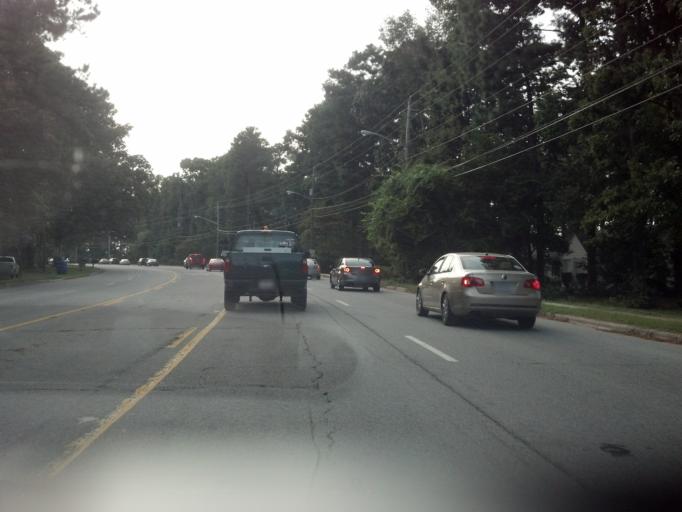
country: US
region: North Carolina
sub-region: Pitt County
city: Greenville
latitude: 35.5906
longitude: -77.3634
